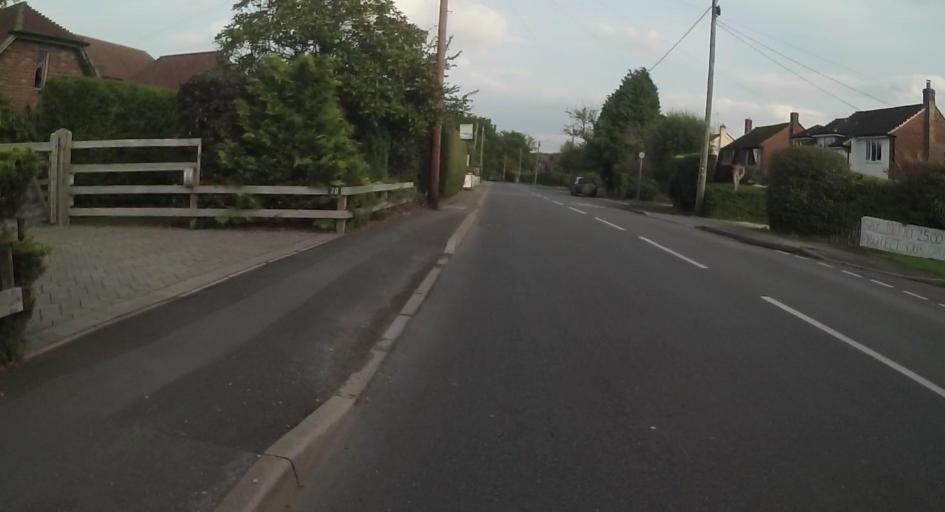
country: GB
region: England
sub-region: West Berkshire
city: Thatcham
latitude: 51.4137
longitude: -1.2219
